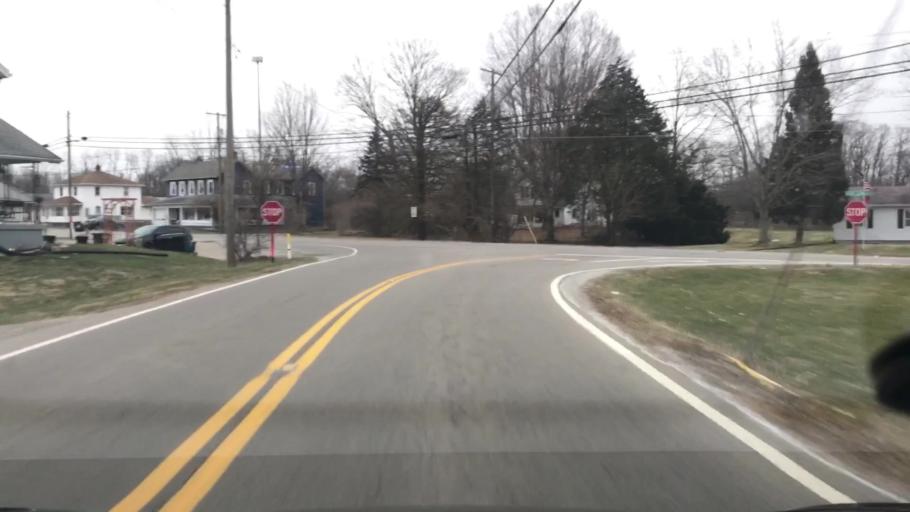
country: US
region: Ohio
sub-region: Clark County
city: Springfield
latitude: 39.8826
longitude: -83.8401
